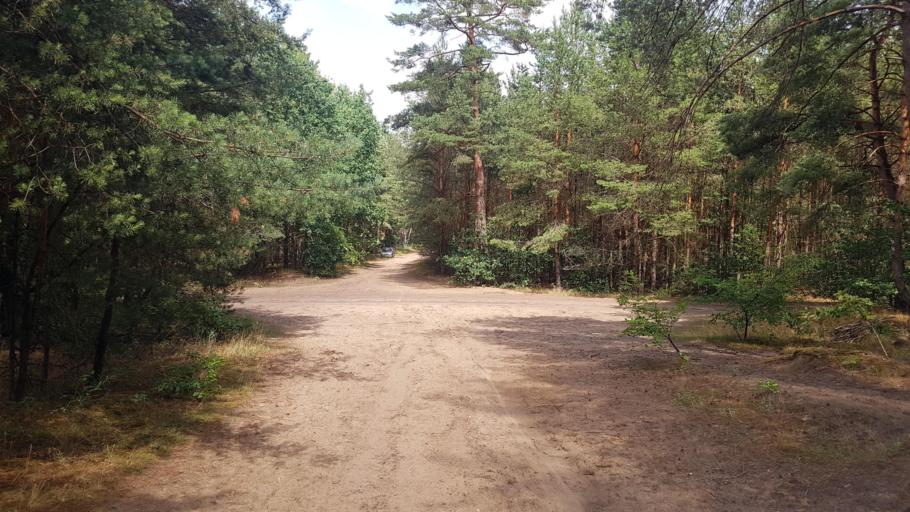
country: DE
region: Brandenburg
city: Trebbin
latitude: 52.2509
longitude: 13.1844
